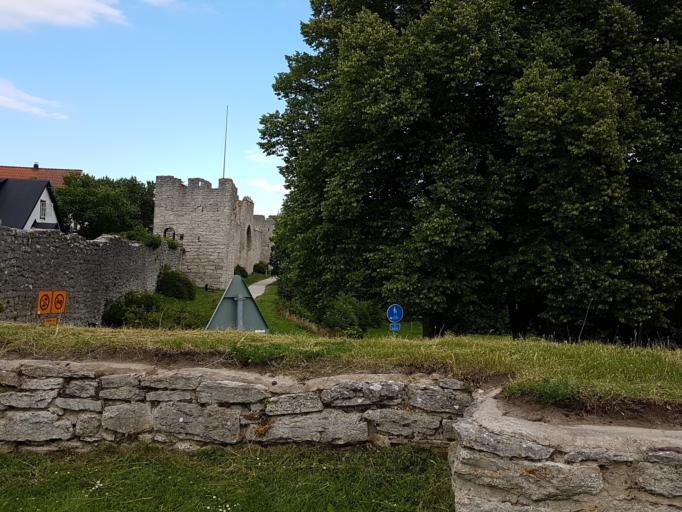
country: SE
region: Gotland
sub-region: Gotland
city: Visby
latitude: 57.6349
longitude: 18.2878
